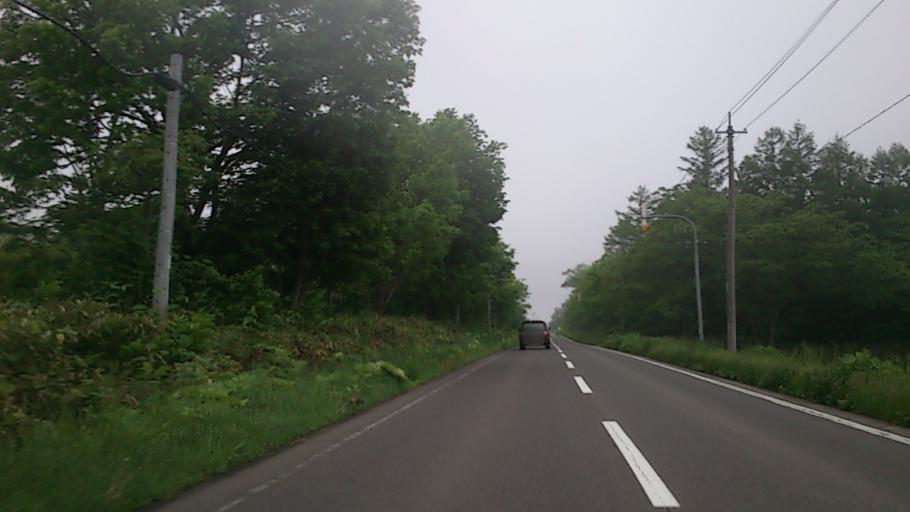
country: JP
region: Hokkaido
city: Niseko Town
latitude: 42.8815
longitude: 140.8020
